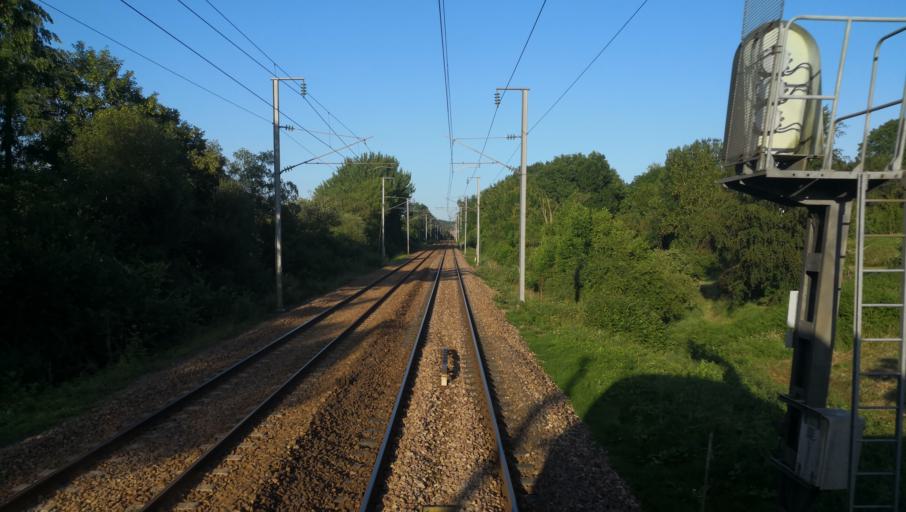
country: FR
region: Lower Normandy
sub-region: Departement du Calvados
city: Beuvillers
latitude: 49.1224
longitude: 0.3171
